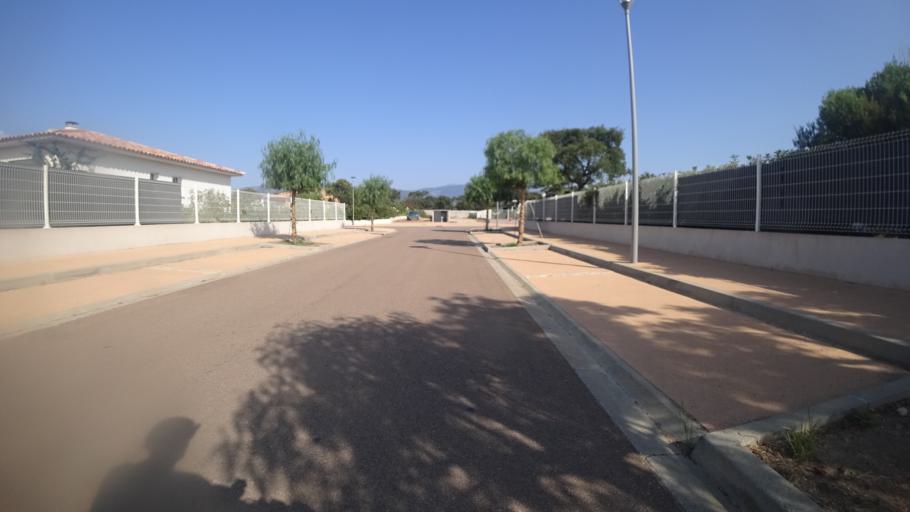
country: FR
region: Corsica
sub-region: Departement de la Corse-du-Sud
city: Porto-Vecchio
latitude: 41.6392
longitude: 9.3387
